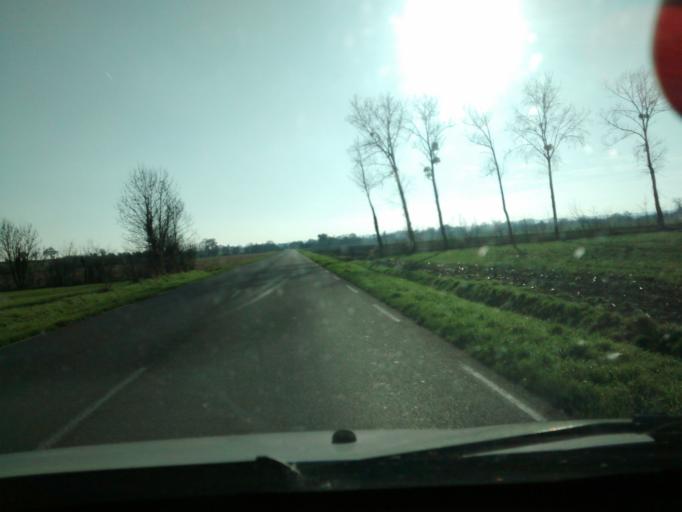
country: FR
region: Lower Normandy
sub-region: Departement de la Manche
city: Pontorson
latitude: 48.5740
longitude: -1.5126
